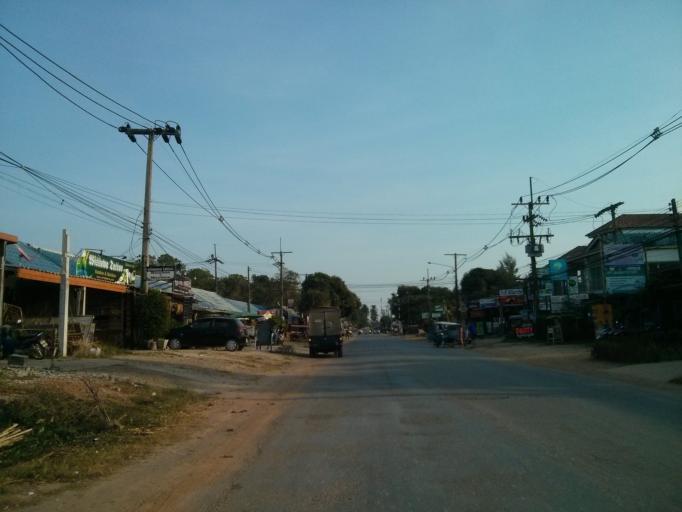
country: TH
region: Krabi
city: Saladan
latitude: 7.5778
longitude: 99.0345
